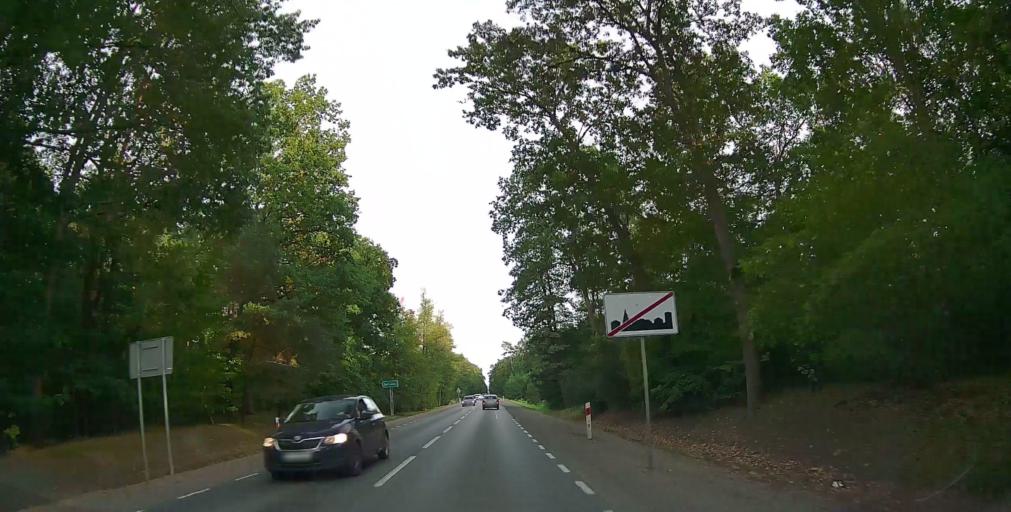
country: PL
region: Masovian Voivodeship
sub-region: Powiat piaseczynski
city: Zabieniec
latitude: 52.0504
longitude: 21.0655
